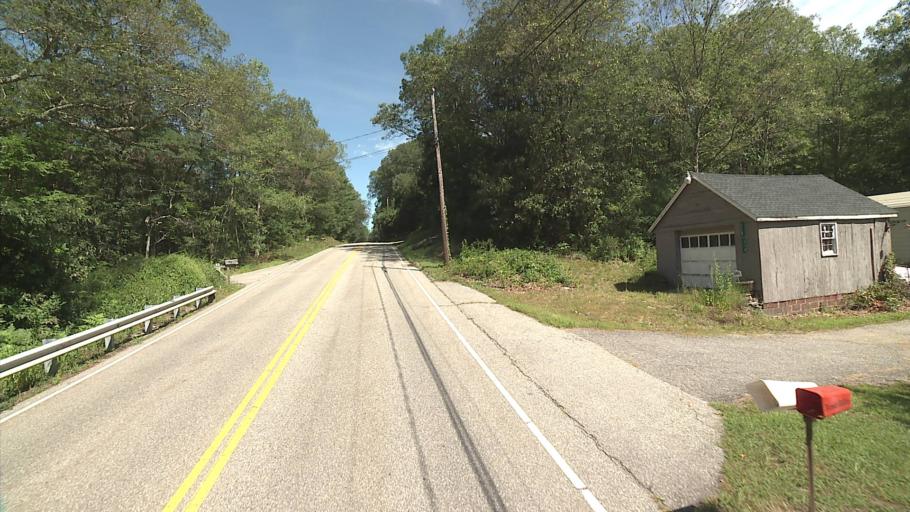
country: US
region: Connecticut
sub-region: New London County
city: Baltic
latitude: 41.6367
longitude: -72.0861
